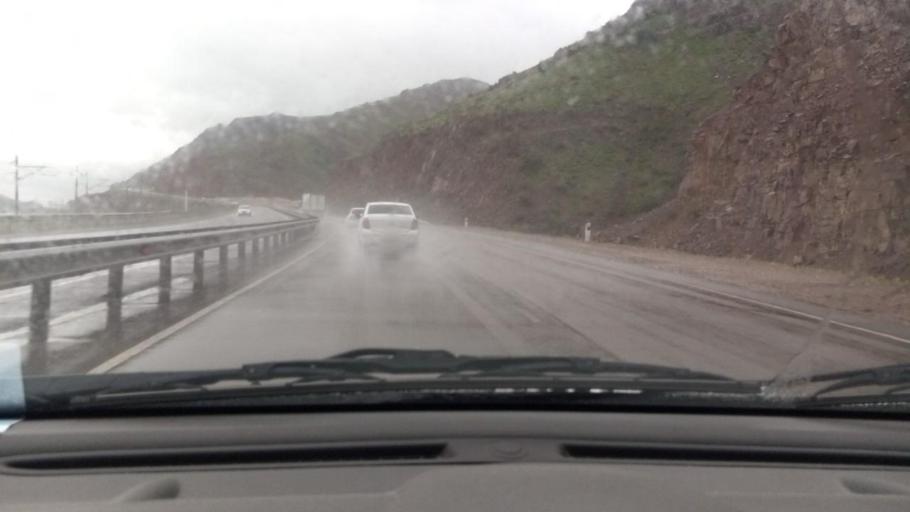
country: UZ
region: Toshkent
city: Angren
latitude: 41.0768
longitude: 70.3022
